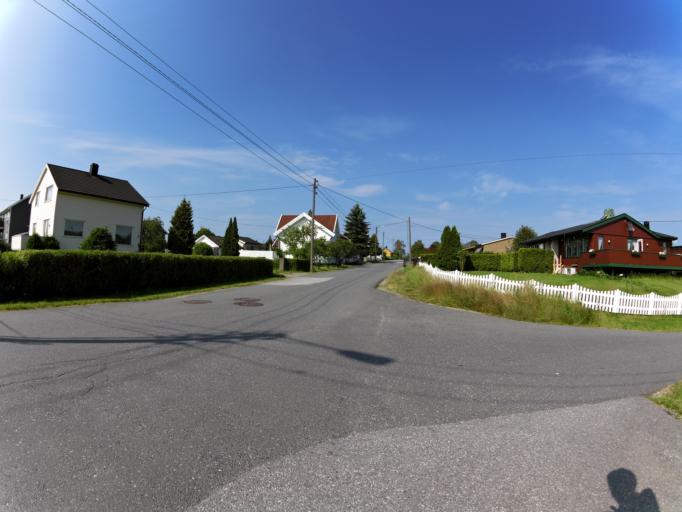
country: NO
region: Ostfold
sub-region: Sarpsborg
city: Sarpsborg
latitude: 59.2613
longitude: 11.0195
